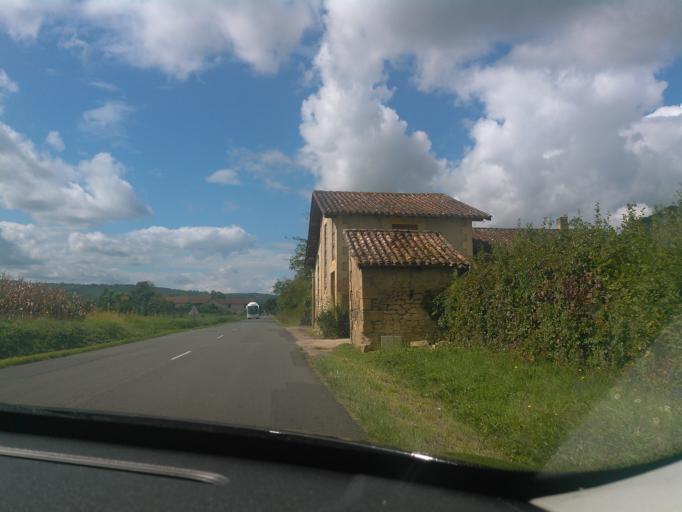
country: FR
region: Aquitaine
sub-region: Departement de la Dordogne
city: Saint-Cyprien
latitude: 44.8374
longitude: 1.1207
